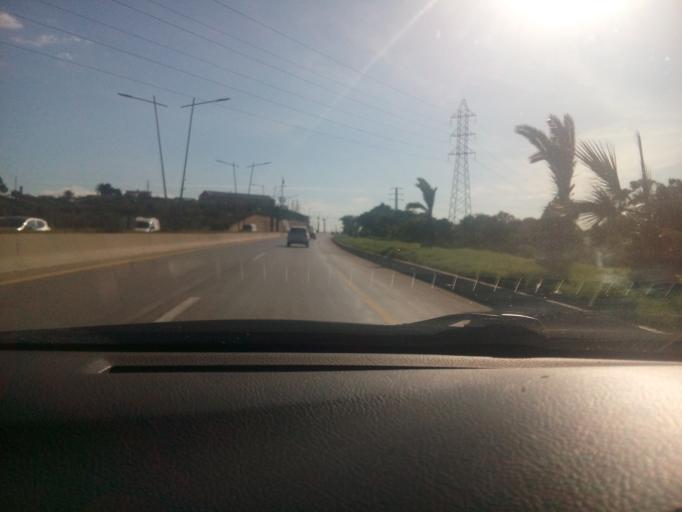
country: DZ
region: Oran
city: Es Senia
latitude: 35.6752
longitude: -0.5977
